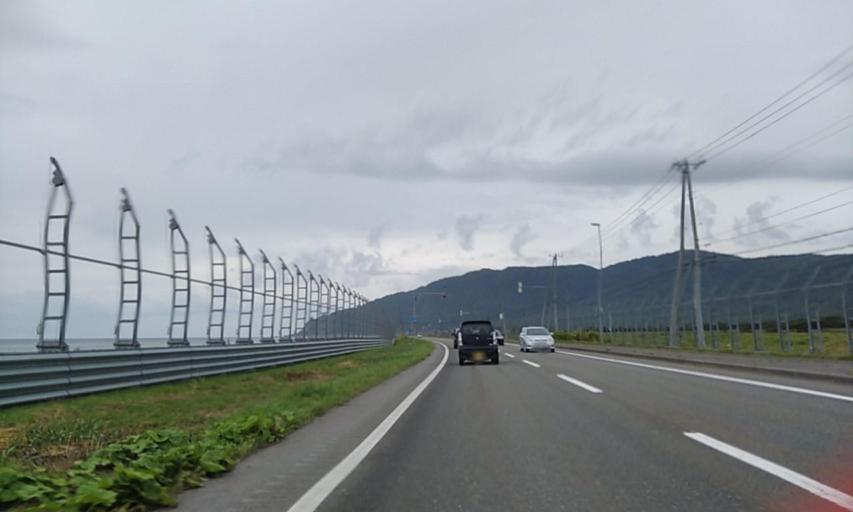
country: JP
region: Hokkaido
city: Makubetsu
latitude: 45.0850
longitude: 142.4522
